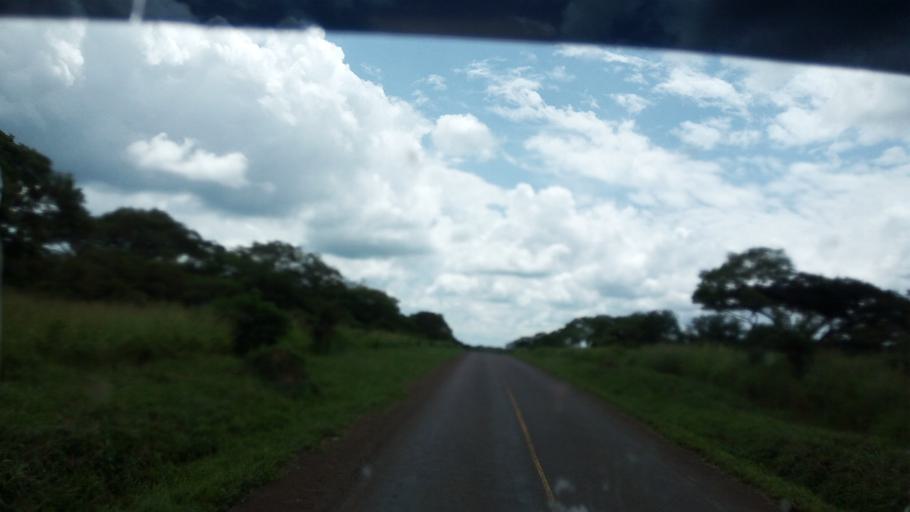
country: UG
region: Northern Region
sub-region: Oyam District
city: Oyam
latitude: 2.3023
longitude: 32.1850
